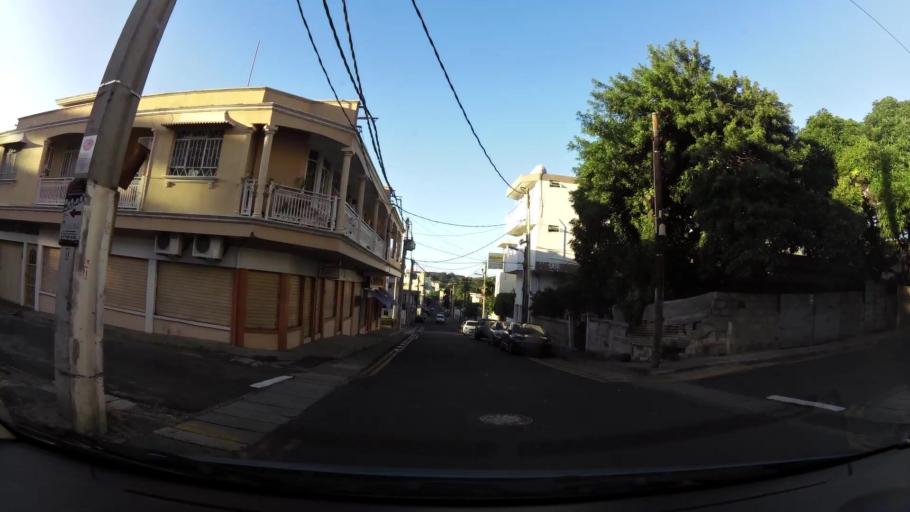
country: MU
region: Port Louis
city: Port Louis
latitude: -20.1730
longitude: 57.5007
